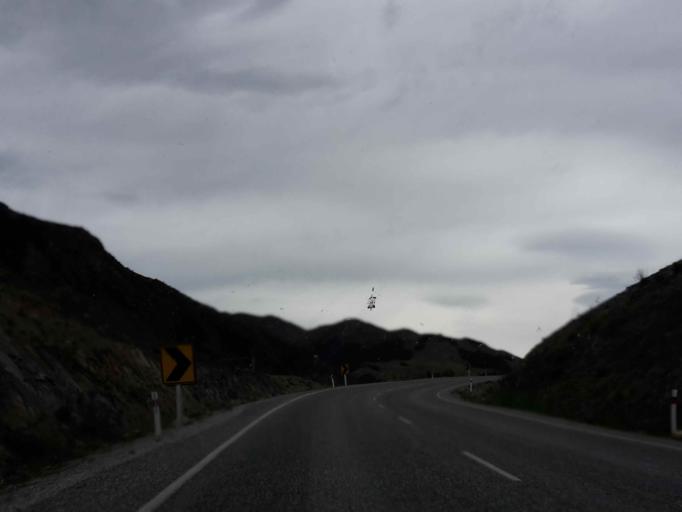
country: NZ
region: Otago
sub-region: Queenstown-Lakes District
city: Wanaka
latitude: -44.6131
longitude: 169.5298
